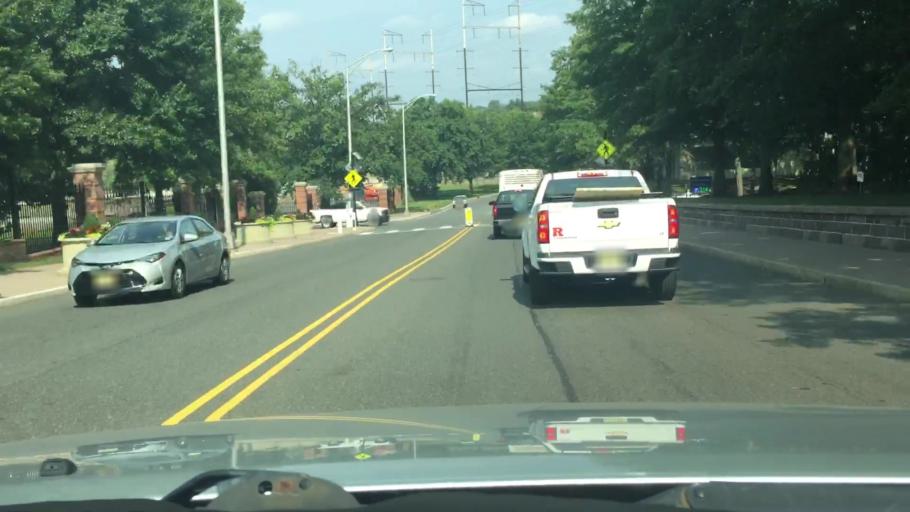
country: US
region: New Jersey
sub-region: Middlesex County
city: New Brunswick
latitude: 40.5000
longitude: -74.4445
